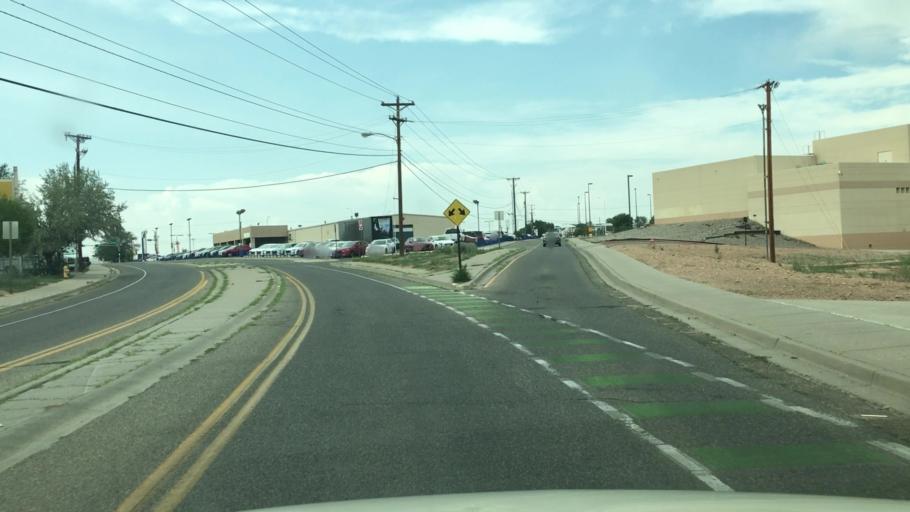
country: US
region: New Mexico
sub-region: Santa Fe County
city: Agua Fria
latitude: 35.6561
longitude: -105.9849
